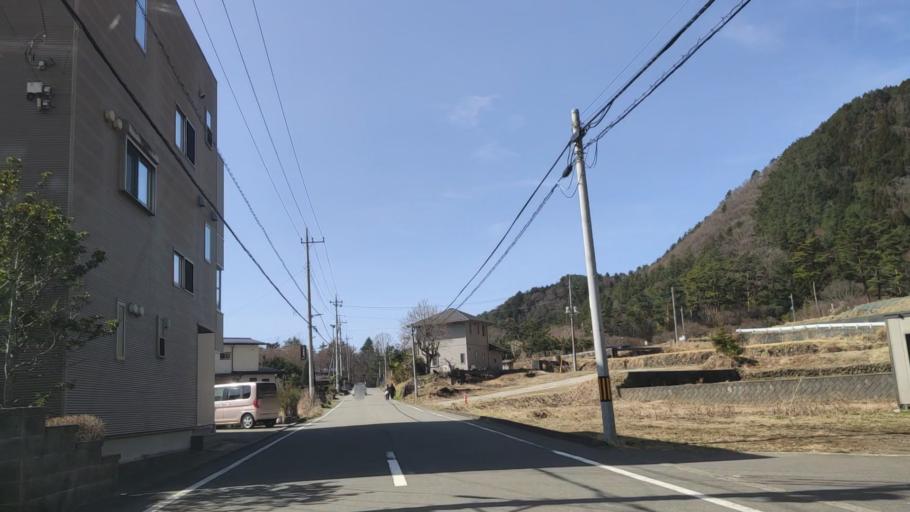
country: JP
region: Yamanashi
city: Fujikawaguchiko
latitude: 35.5276
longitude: 138.7632
